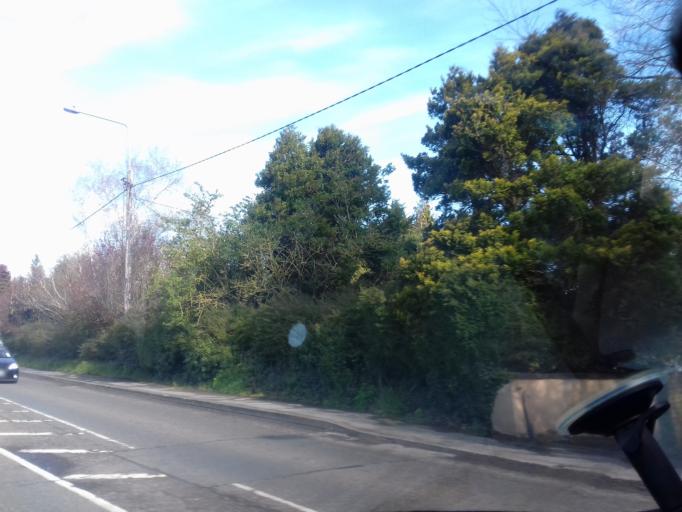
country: IE
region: Leinster
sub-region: An Mhi
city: Kells
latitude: 53.7249
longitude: -6.8657
